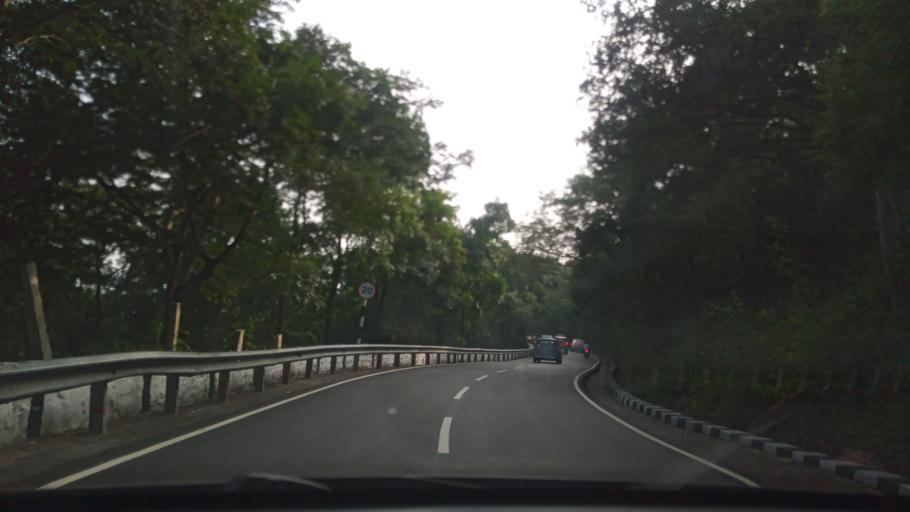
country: IN
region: Andhra Pradesh
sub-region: Chittoor
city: Akkarampalle
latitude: 13.6537
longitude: 79.4119
